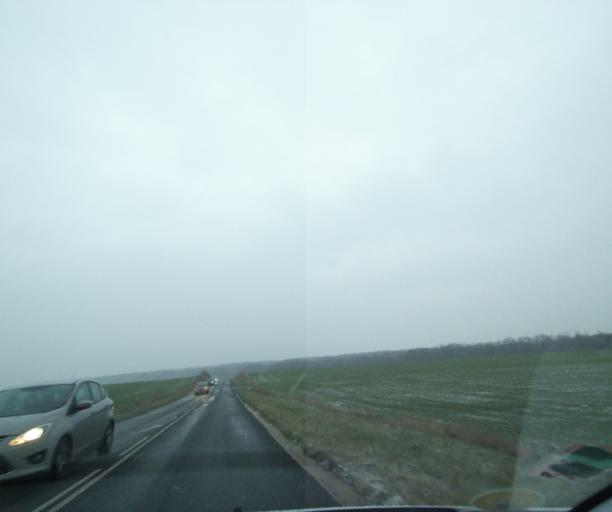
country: FR
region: Champagne-Ardenne
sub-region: Departement de la Haute-Marne
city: Wassy
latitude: 48.4794
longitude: 5.0056
